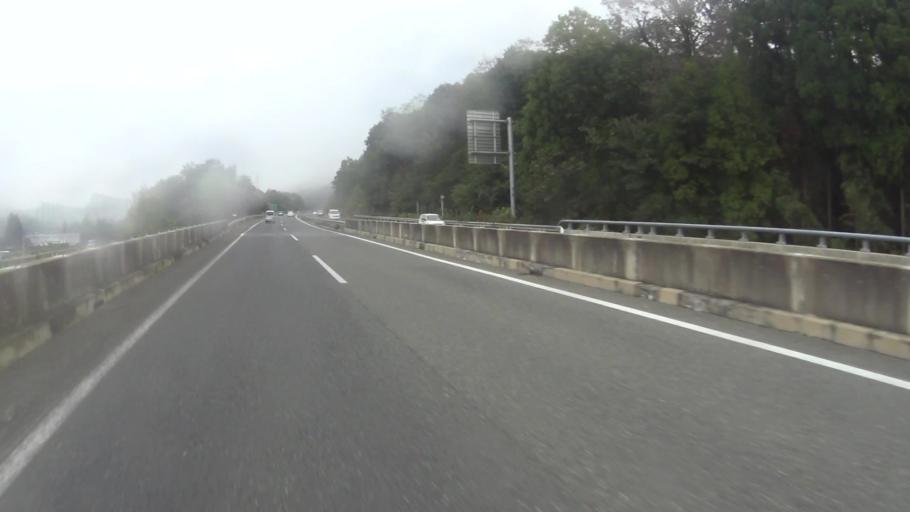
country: JP
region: Kyoto
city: Kameoka
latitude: 35.0946
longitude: 135.4990
